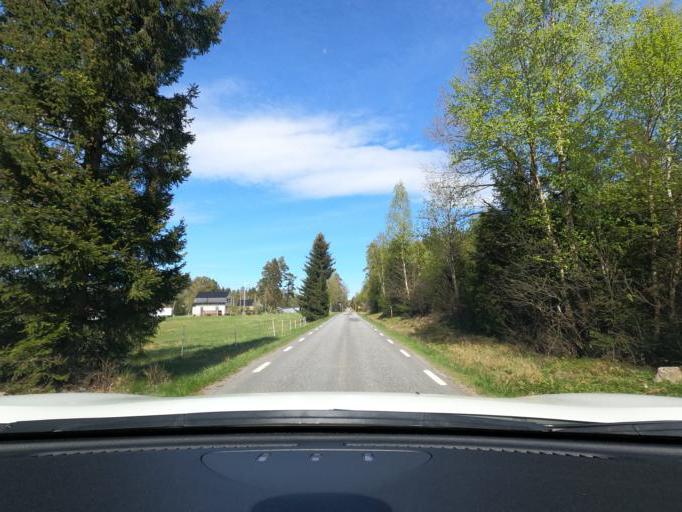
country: SE
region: Vaestra Goetaland
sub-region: Marks Kommun
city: Horred
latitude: 57.4460
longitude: 12.4370
